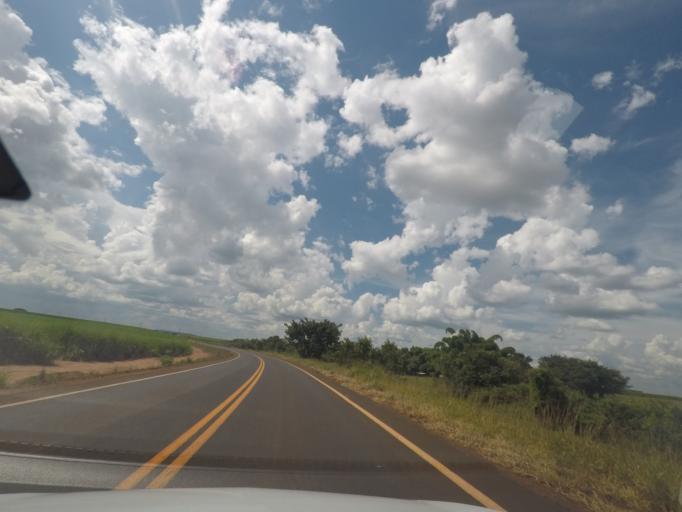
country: BR
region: Minas Gerais
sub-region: Conceicao Das Alagoas
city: Conceicao das Alagoas
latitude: -19.8345
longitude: -48.5897
